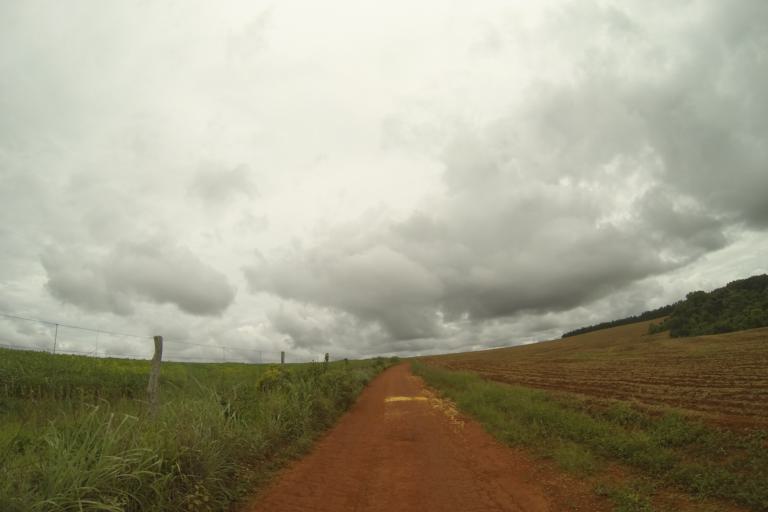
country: BR
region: Minas Gerais
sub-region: Ibia
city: Ibia
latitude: -19.7173
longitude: -46.5798
